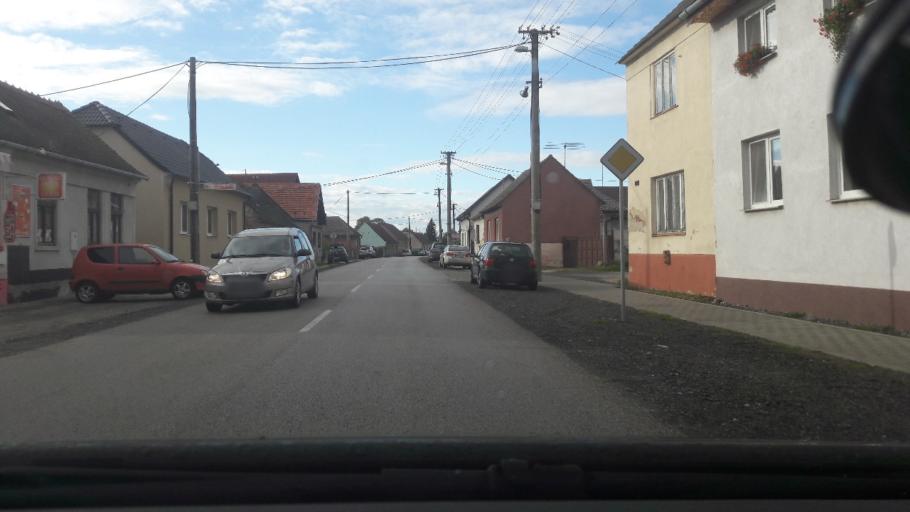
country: CZ
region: South Moravian
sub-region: Okres Breclav
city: Lanzhot
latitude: 48.6599
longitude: 17.0176
